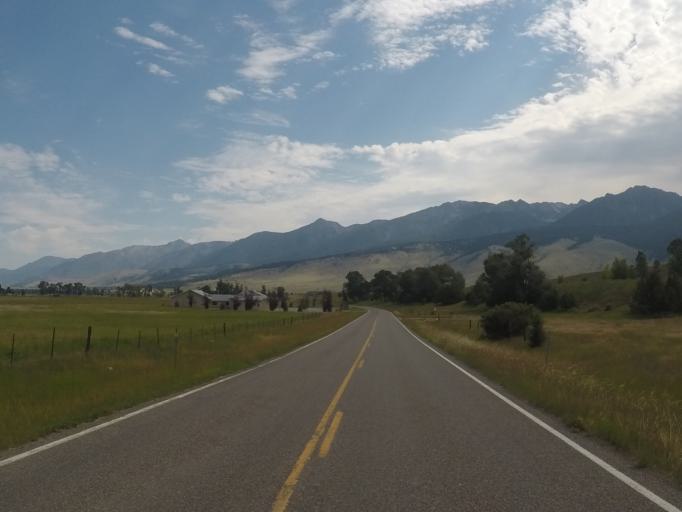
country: US
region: Montana
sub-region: Park County
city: Livingston
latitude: 45.4197
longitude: -110.6340
